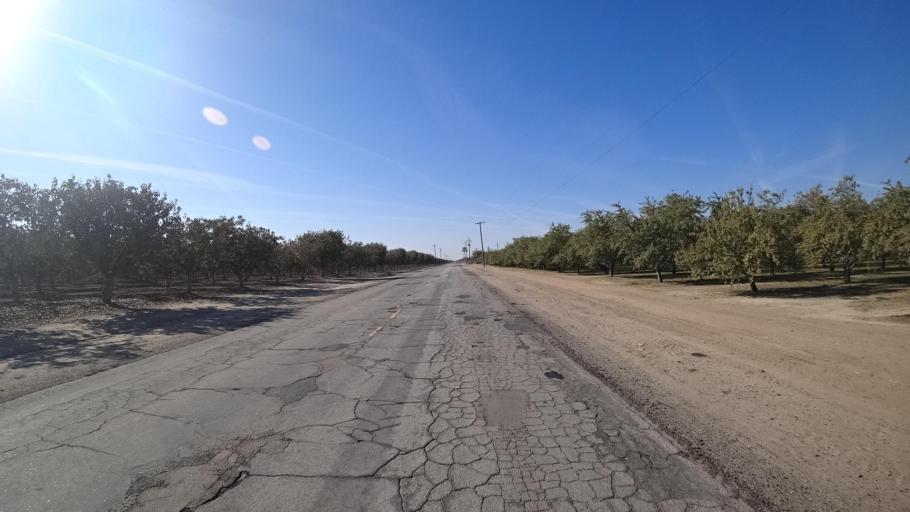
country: US
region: California
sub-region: Kern County
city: Wasco
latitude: 35.6524
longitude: -119.3376
